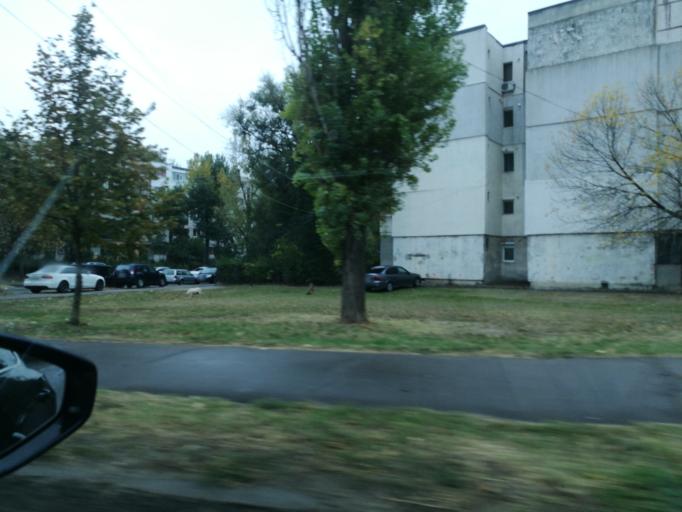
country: RO
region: Galati
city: Galati
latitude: 45.4574
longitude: 28.0181
